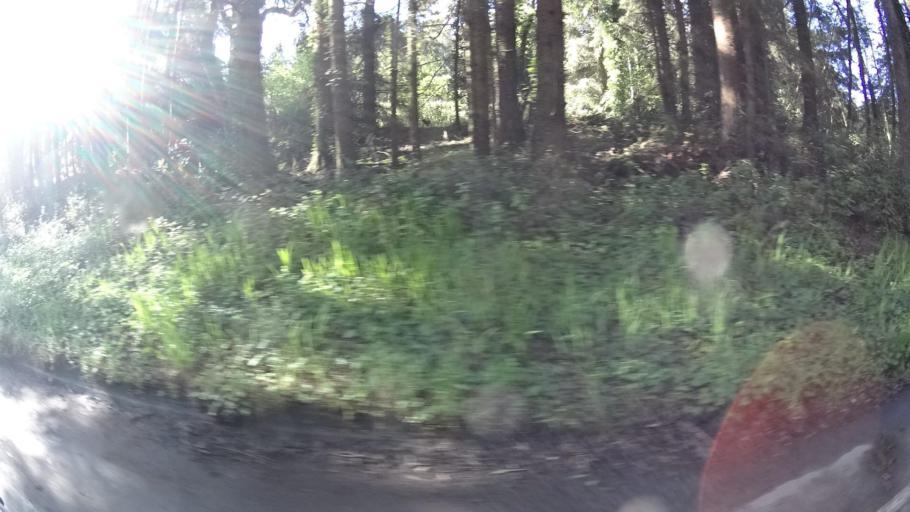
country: US
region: California
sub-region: Humboldt County
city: Westhaven-Moonstone
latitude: 41.1363
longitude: -124.1478
